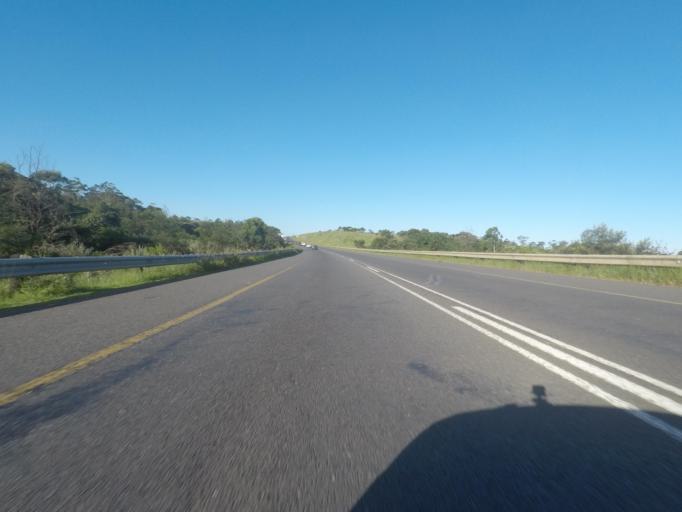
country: ZA
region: Eastern Cape
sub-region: Buffalo City Metropolitan Municipality
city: East London
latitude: -33.0438
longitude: 27.8280
